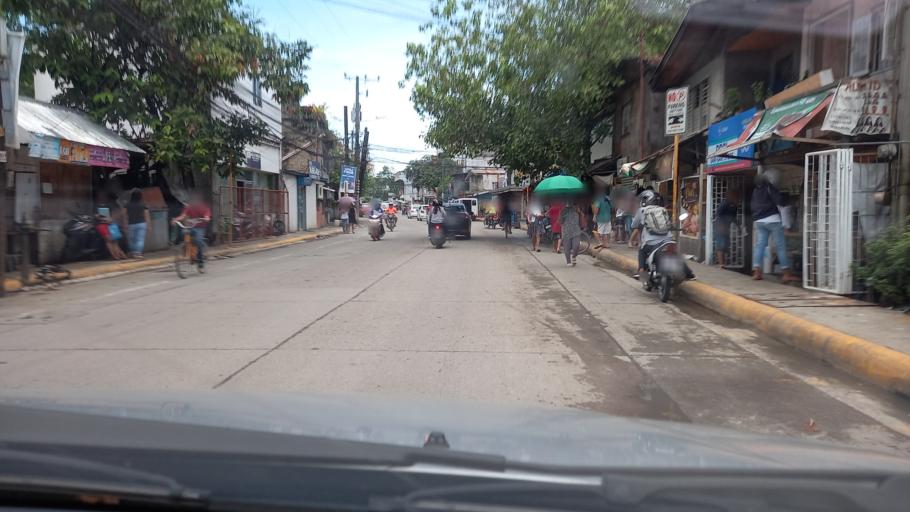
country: PH
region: Central Visayas
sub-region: Lapu-Lapu City
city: Buagsong
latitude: 10.3250
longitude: 123.9416
